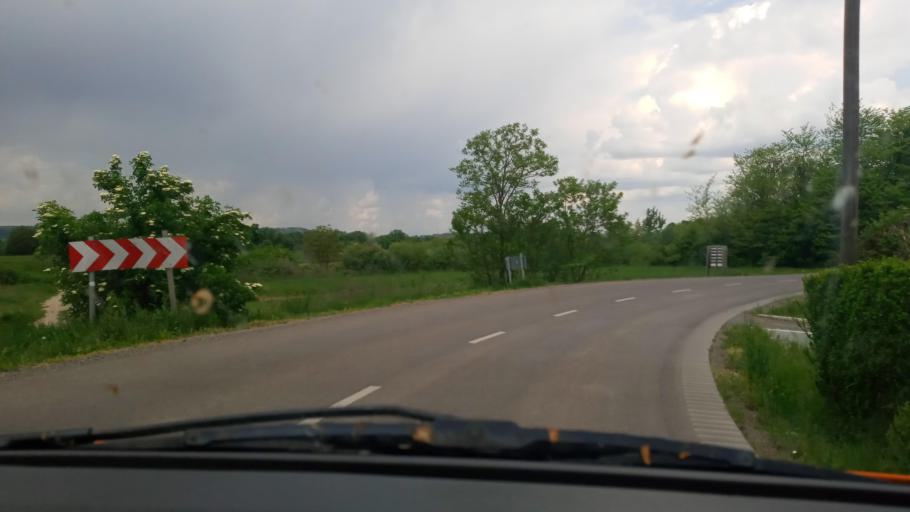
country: HU
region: Baranya
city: Villany
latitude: 45.8518
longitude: 18.4804
